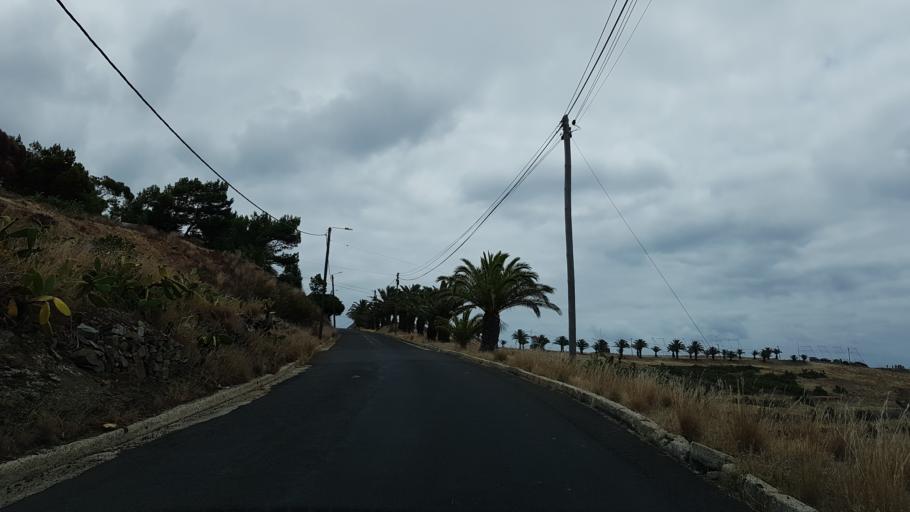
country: PT
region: Madeira
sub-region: Porto Santo
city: Vila de Porto Santo
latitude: 33.0688
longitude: -16.3201
